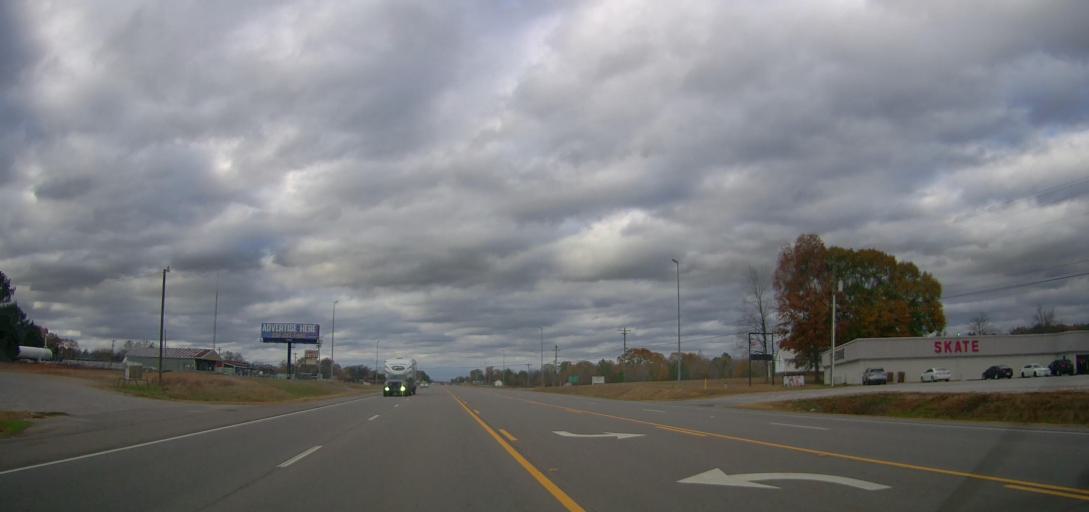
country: US
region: Alabama
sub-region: Lawrence County
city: Moulton
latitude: 34.5093
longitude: -87.2884
